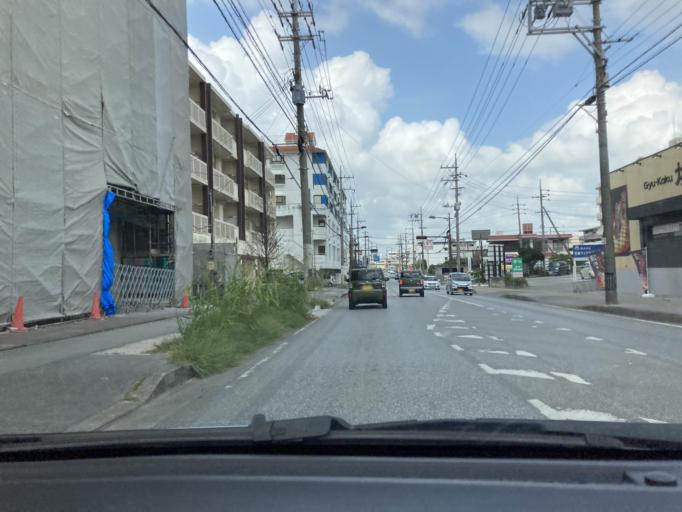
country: JP
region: Okinawa
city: Ginowan
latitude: 26.2501
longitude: 127.7716
